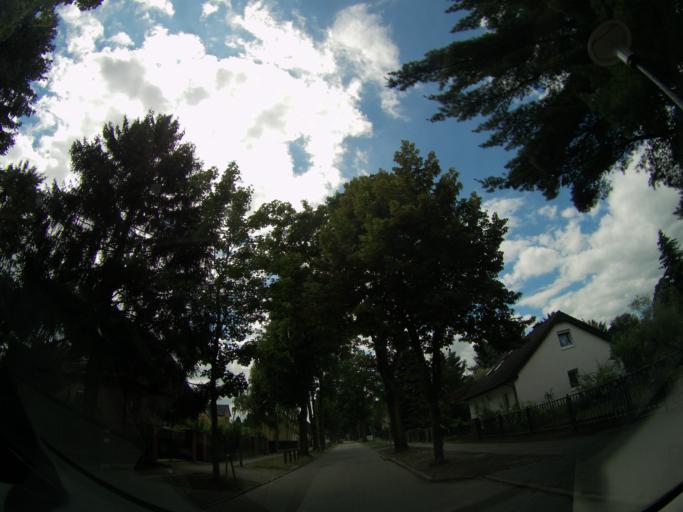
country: DE
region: Brandenburg
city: Teltow
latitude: 52.3973
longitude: 13.2873
